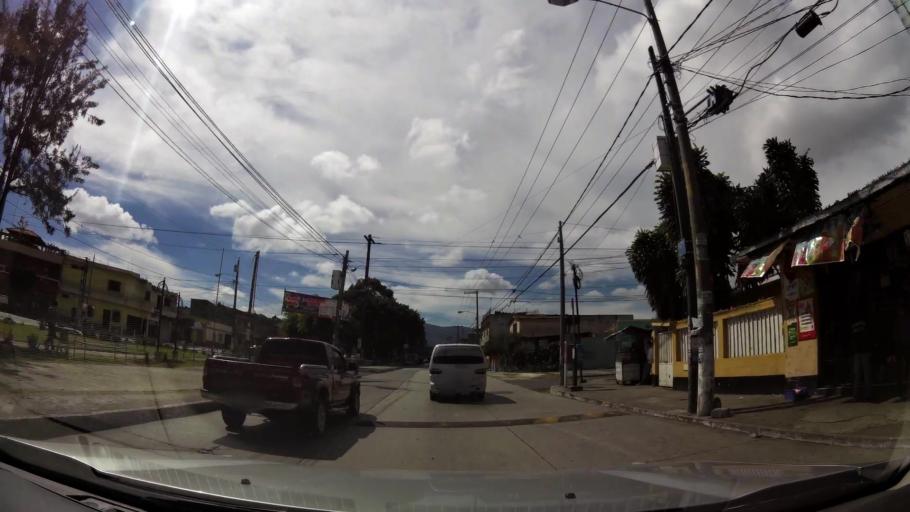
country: GT
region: Guatemala
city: Mixco
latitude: 14.6502
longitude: -90.5785
